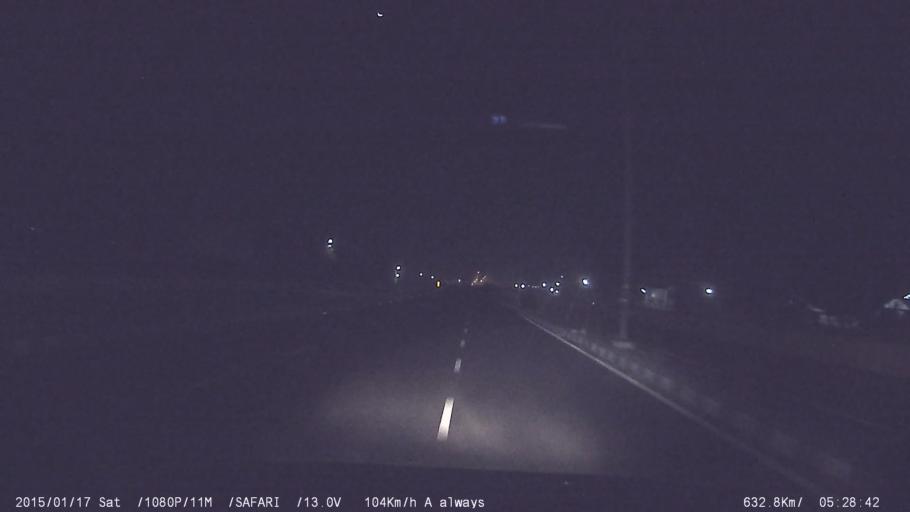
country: IN
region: Tamil Nadu
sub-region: Vellore
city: Arcot
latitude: 12.9233
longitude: 79.2757
